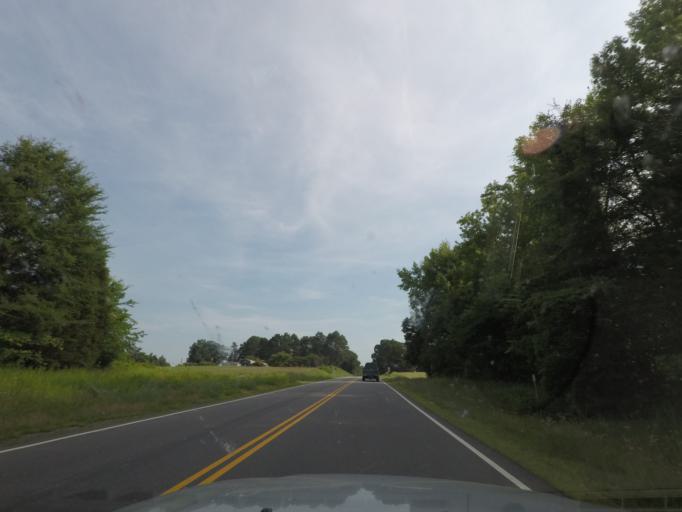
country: US
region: Virginia
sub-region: Mecklenburg County
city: Chase City
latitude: 36.8144
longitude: -78.5992
